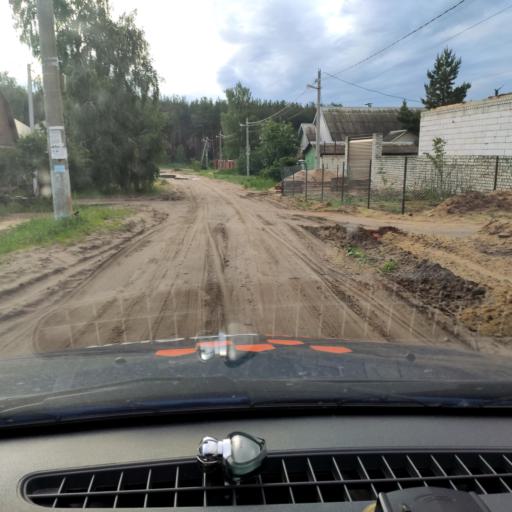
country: RU
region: Voronezj
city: Somovo
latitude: 51.7541
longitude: 39.3232
